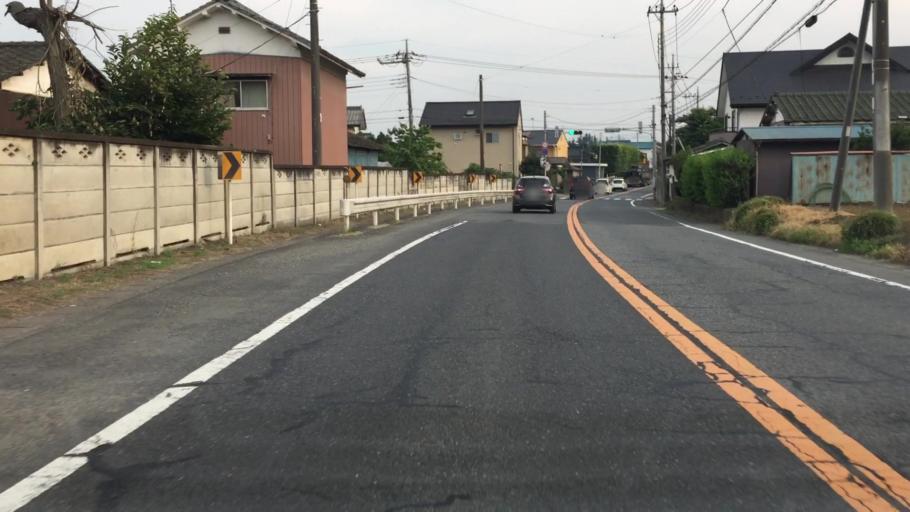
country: JP
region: Tochigi
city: Fujioka
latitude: 36.2887
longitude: 139.6667
